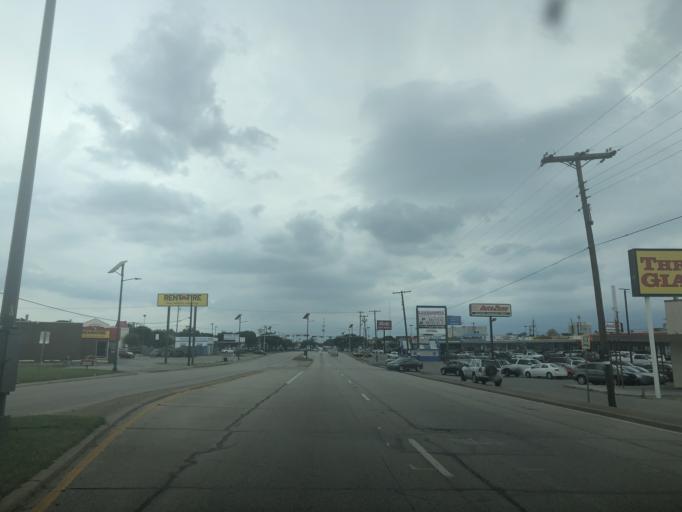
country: US
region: Texas
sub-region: Dallas County
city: Irving
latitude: 32.8106
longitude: -96.9324
